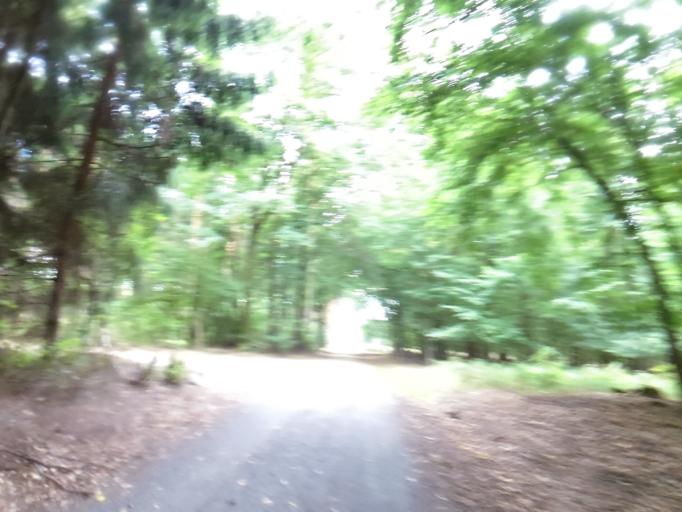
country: DE
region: Hesse
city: Morfelden-Walldorf
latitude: 50.0088
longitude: 8.5534
